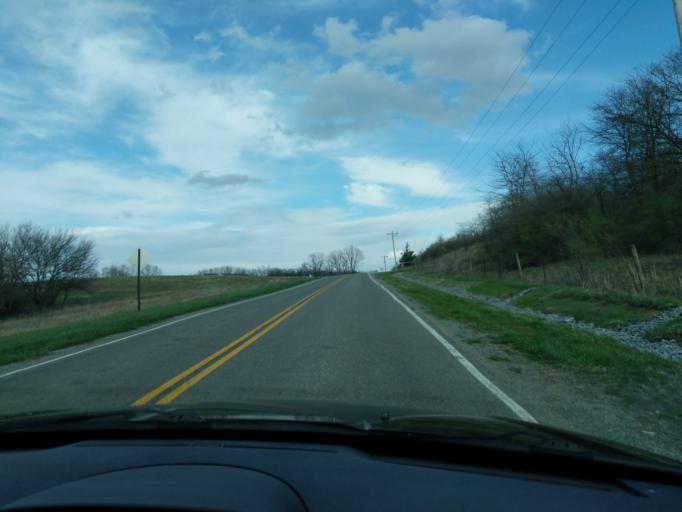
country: US
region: Ohio
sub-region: Champaign County
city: Urbana
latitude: 40.1559
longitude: -83.6688
